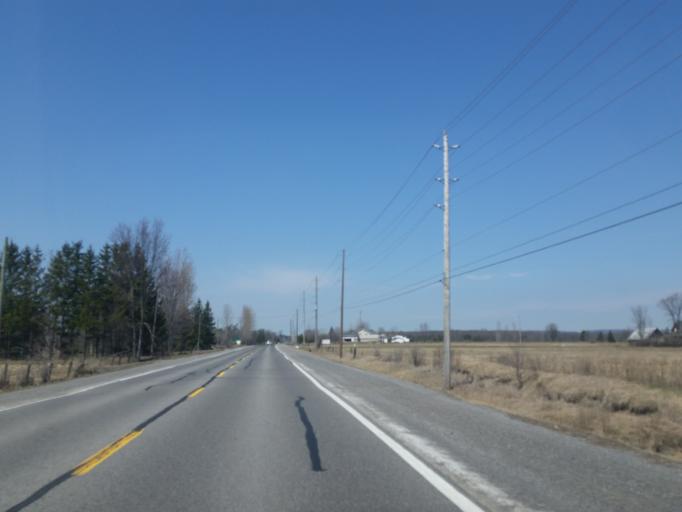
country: CA
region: Ontario
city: Bells Corners
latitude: 45.4515
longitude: -76.0610
